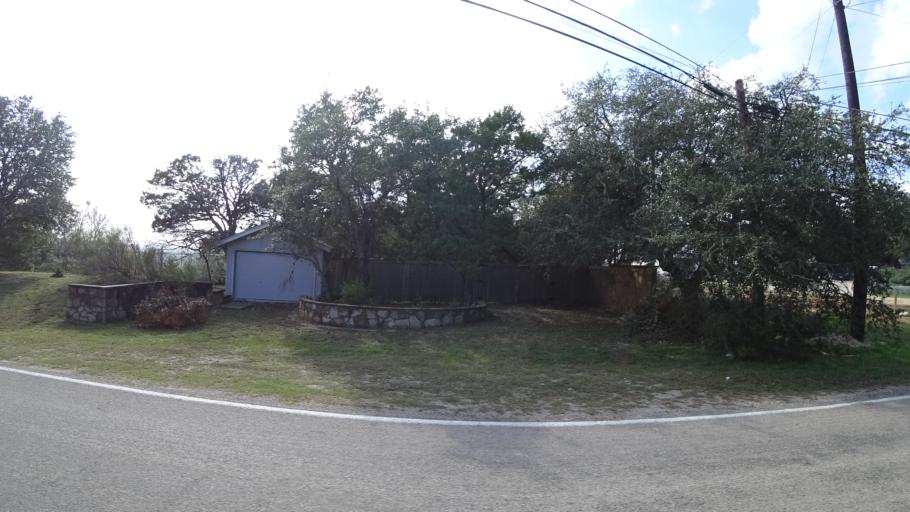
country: US
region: Texas
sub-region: Travis County
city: Barton Creek
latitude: 30.3067
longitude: -97.8653
